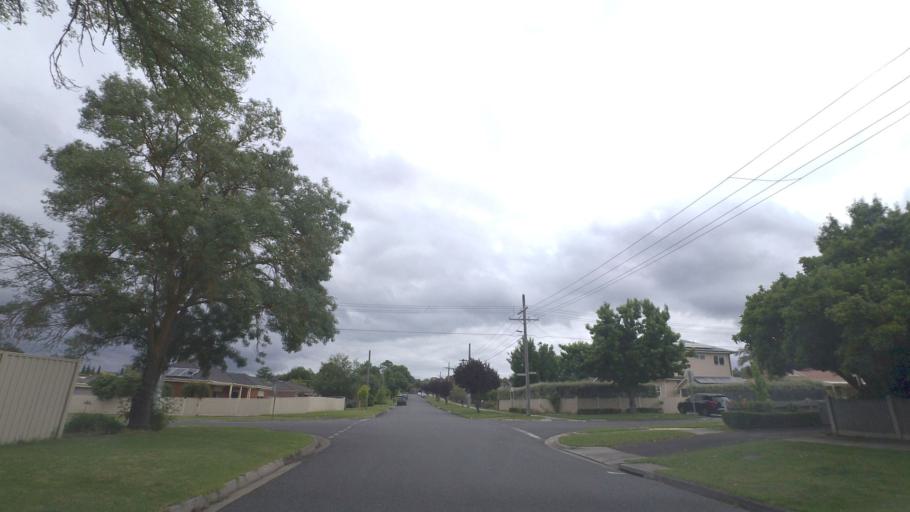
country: AU
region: Victoria
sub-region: Yarra Ranges
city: Lilydale
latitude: -37.7509
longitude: 145.3400
